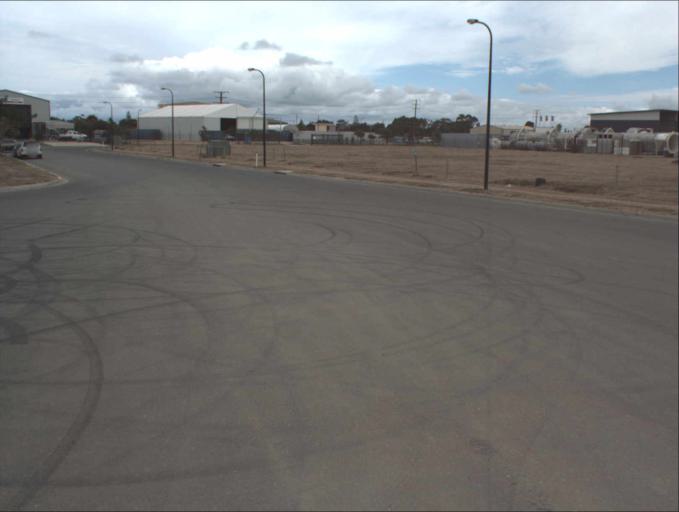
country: AU
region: South Australia
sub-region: Port Adelaide Enfield
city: Birkenhead
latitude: -34.8203
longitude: 138.5096
